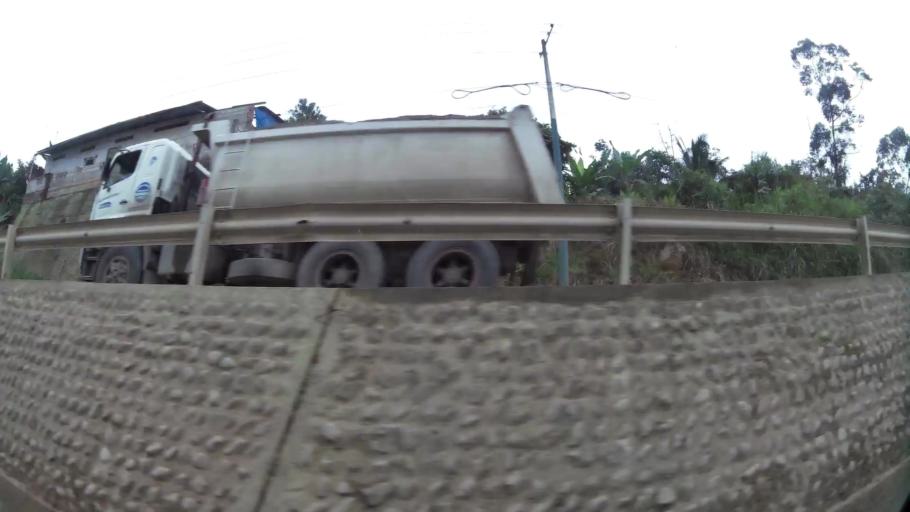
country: EC
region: El Oro
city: Pasaje
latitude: -3.3321
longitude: -79.7852
